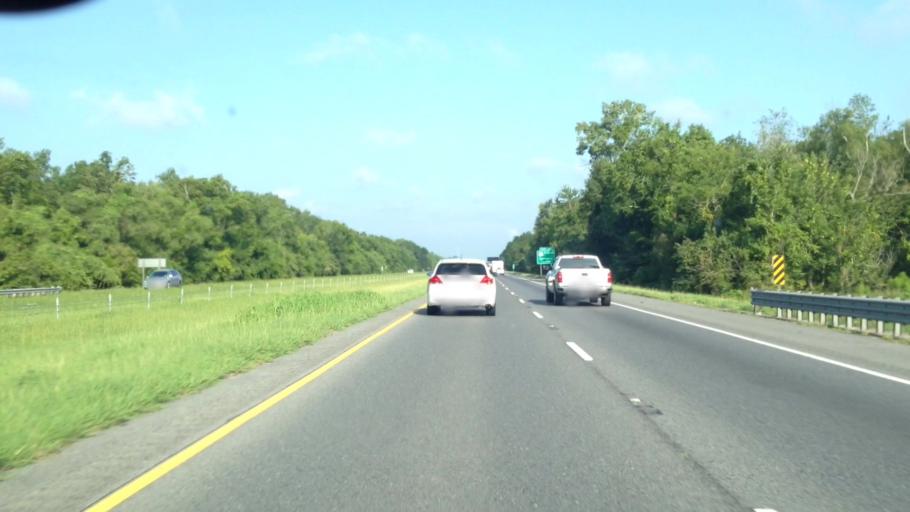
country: US
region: Louisiana
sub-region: Ascension Parish
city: Sorrento
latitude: 30.1509
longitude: -90.7888
